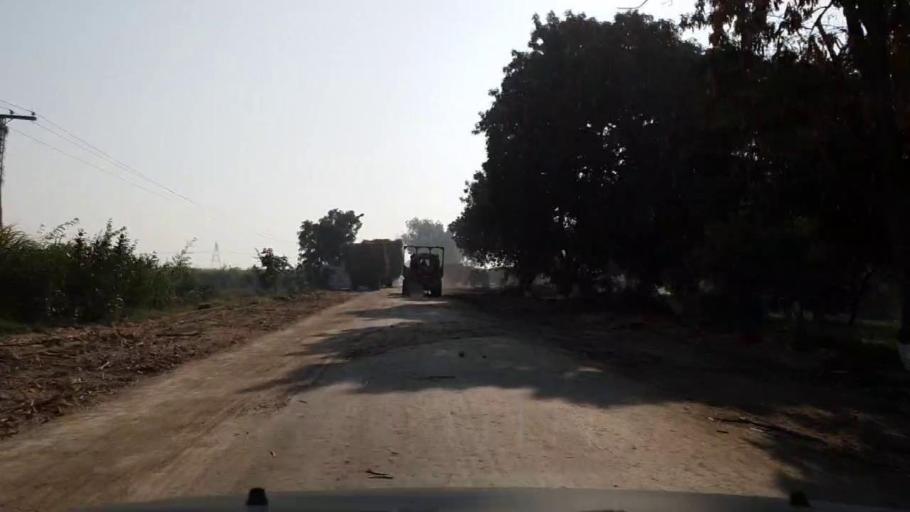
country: PK
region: Sindh
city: Matiari
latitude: 25.5776
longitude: 68.5021
